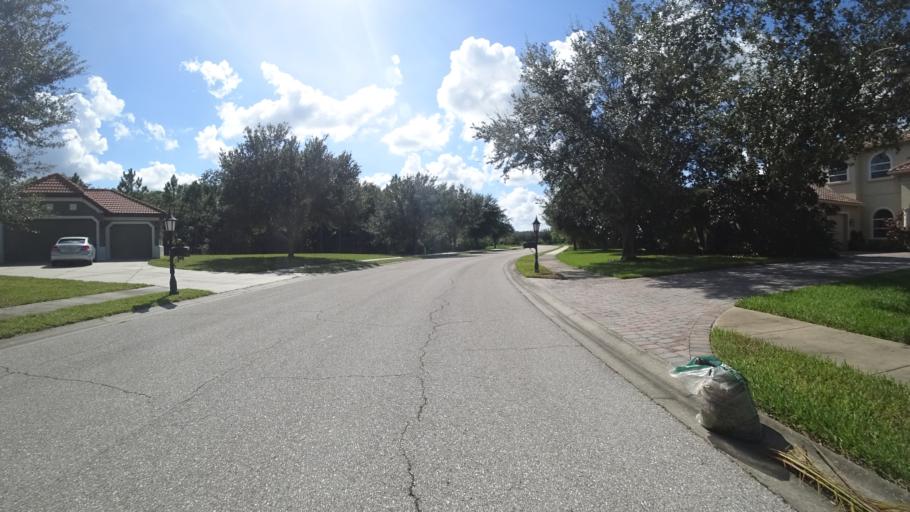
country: US
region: Florida
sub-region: Manatee County
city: Ellenton
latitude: 27.4992
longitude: -82.3734
